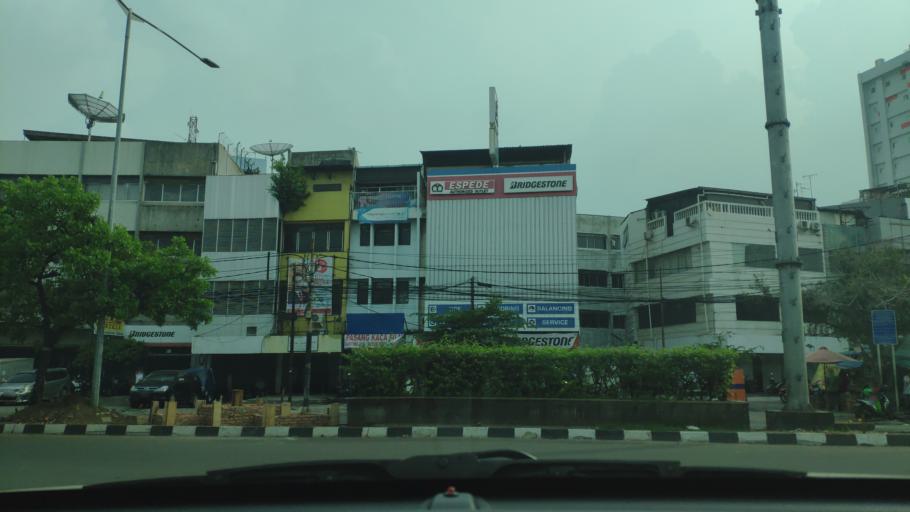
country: ID
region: Jakarta Raya
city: Jakarta
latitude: -6.1596
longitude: 106.8210
